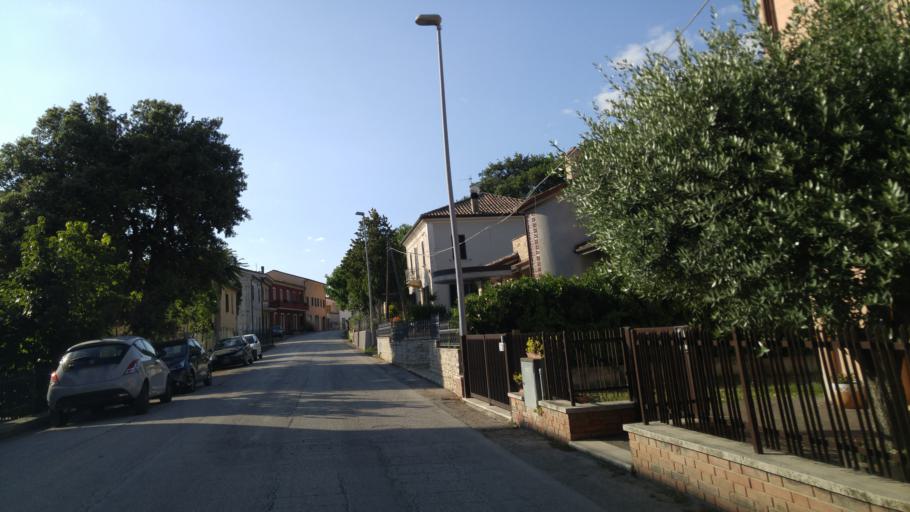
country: IT
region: The Marches
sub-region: Provincia di Pesaro e Urbino
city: Sant'Ippolito
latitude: 43.6831
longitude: 12.8715
